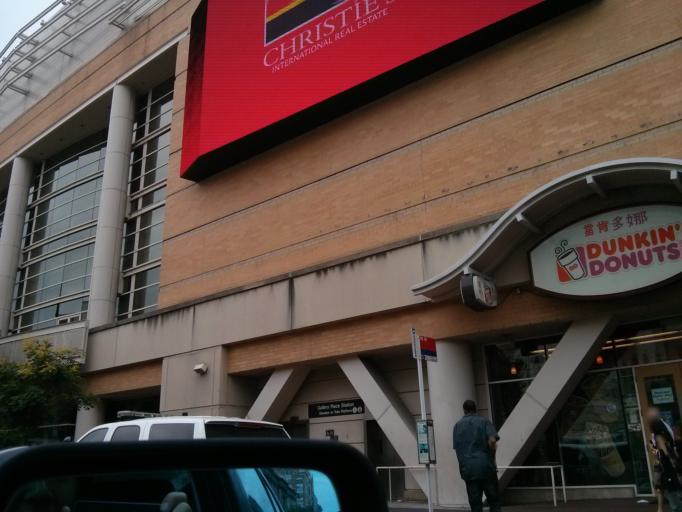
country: US
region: Washington, D.C.
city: Washington, D.C.
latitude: 38.8982
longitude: -77.0219
